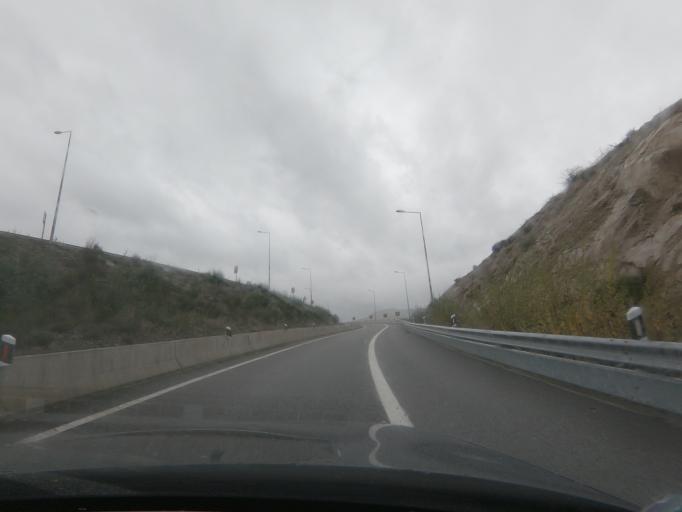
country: PT
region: Vila Real
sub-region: Vila Real
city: Vila Real
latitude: 41.2772
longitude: -7.7690
